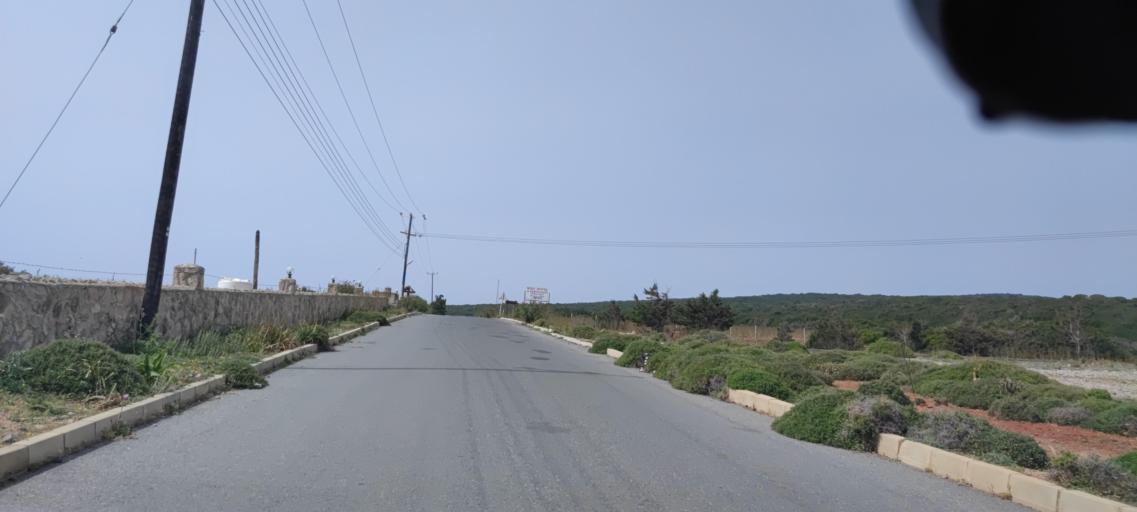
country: CY
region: Ammochostos
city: Rizokarpaso
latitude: 35.6570
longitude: 34.5719
